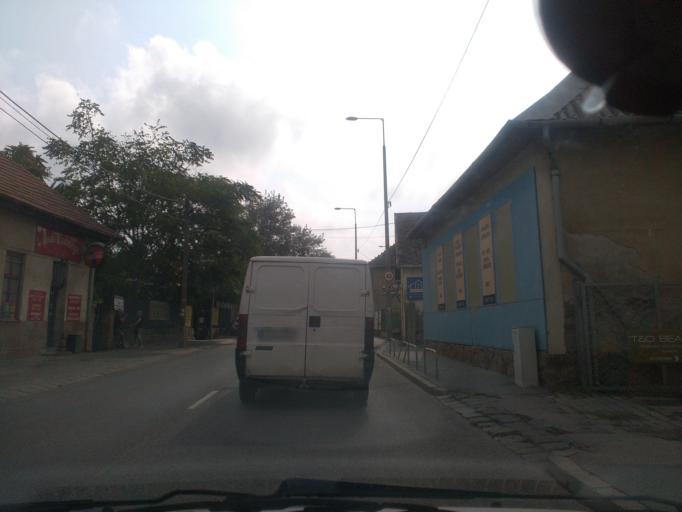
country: HU
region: Pest
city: Solymar
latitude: 47.5643
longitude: 18.9611
